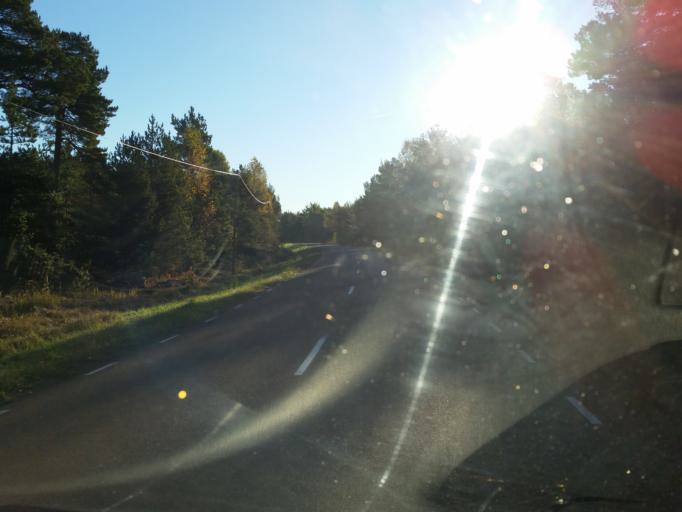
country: AX
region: Alands skaergard
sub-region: Vardoe
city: Vardoe
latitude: 60.2283
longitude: 20.3987
